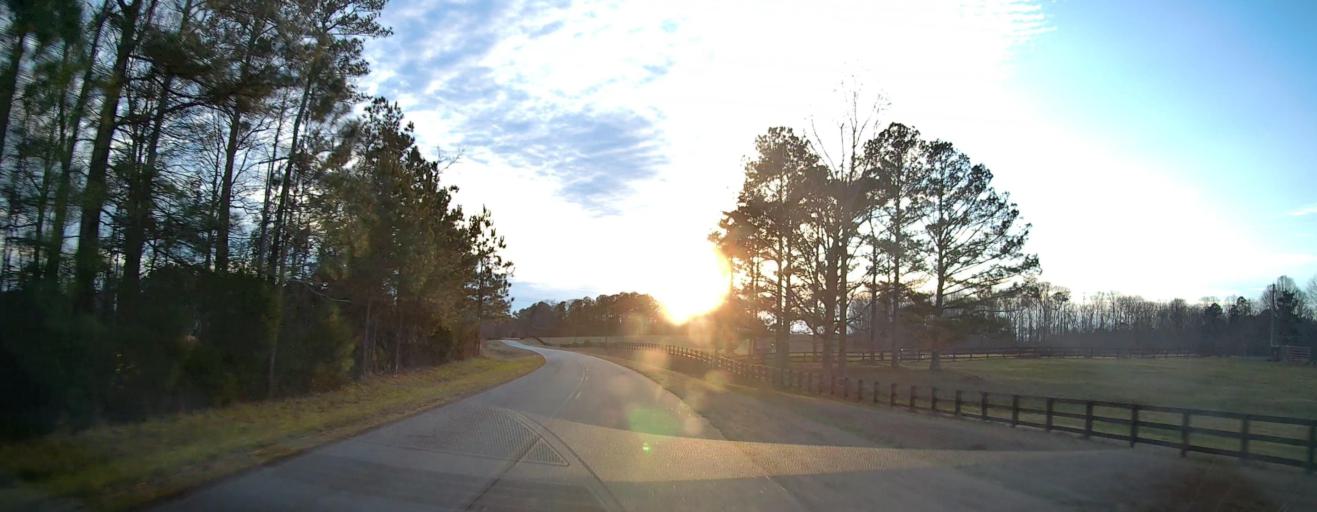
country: US
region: Georgia
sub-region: Harris County
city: Hamilton
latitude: 32.6048
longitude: -84.8748
